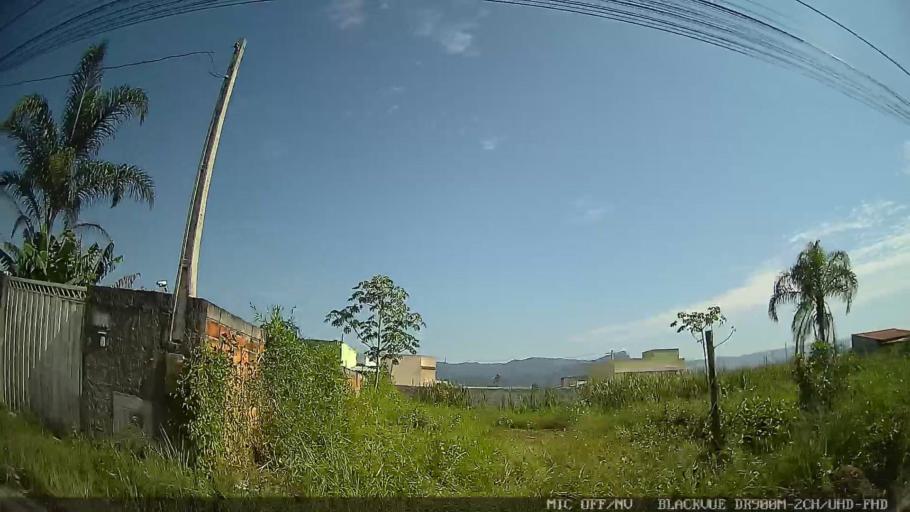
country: BR
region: Sao Paulo
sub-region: Caraguatatuba
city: Caraguatatuba
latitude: -23.6720
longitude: -45.4561
